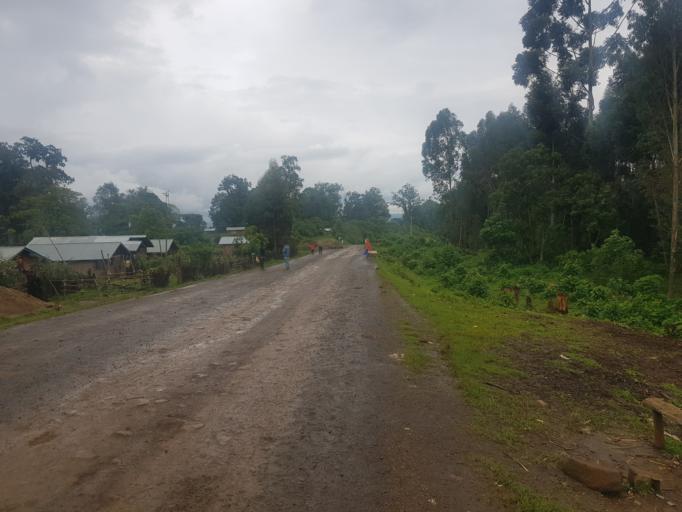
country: ET
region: Oromiya
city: Gore
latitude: 7.6775
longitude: 35.4994
